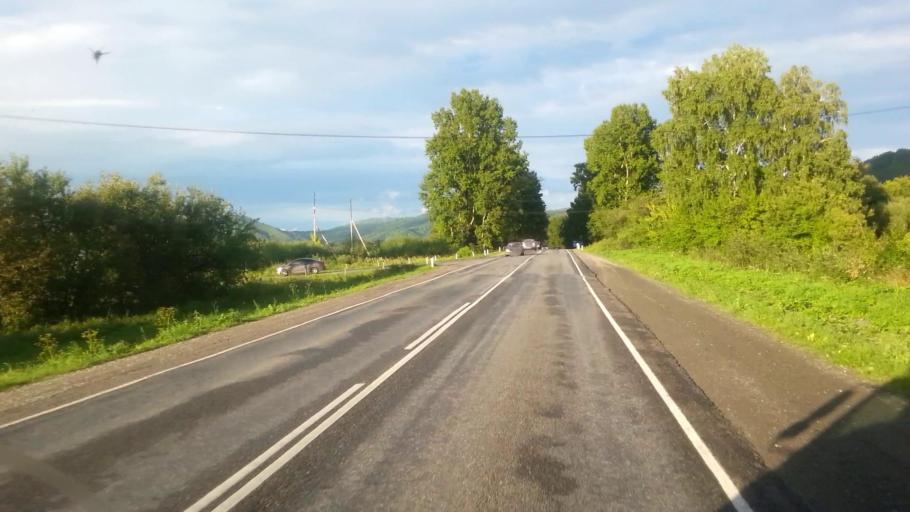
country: RU
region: Altay
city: Souzga
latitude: 51.8786
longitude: 85.8214
